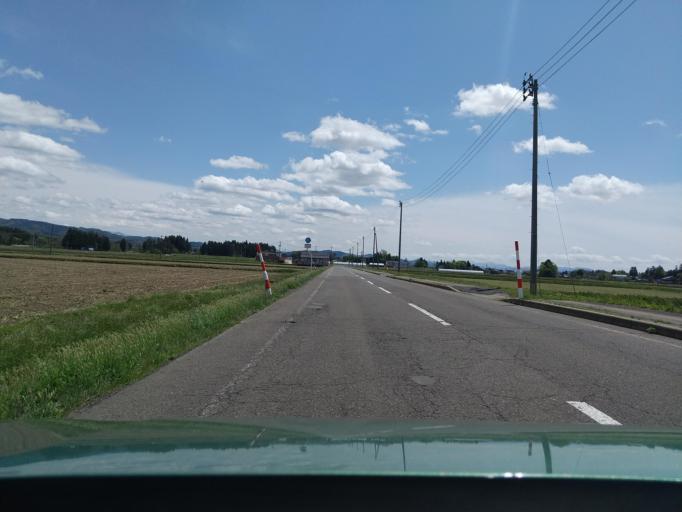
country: JP
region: Akita
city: Yokotemachi
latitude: 39.3632
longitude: 140.5365
